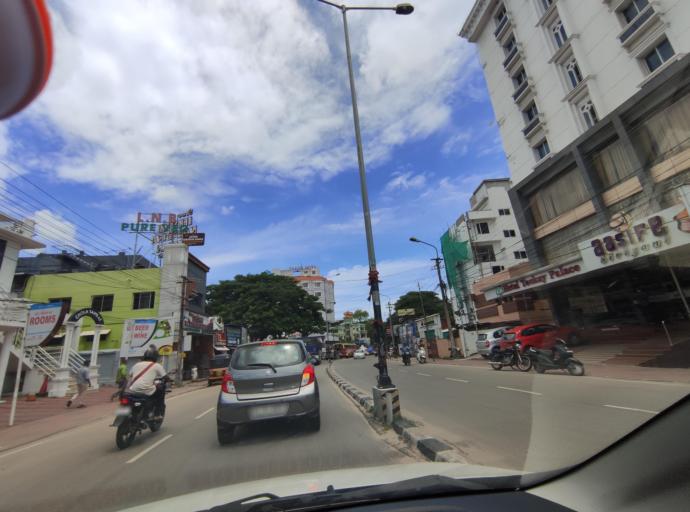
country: IN
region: Kerala
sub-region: Thiruvananthapuram
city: Thiruvananthapuram
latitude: 8.4896
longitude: 76.9539
